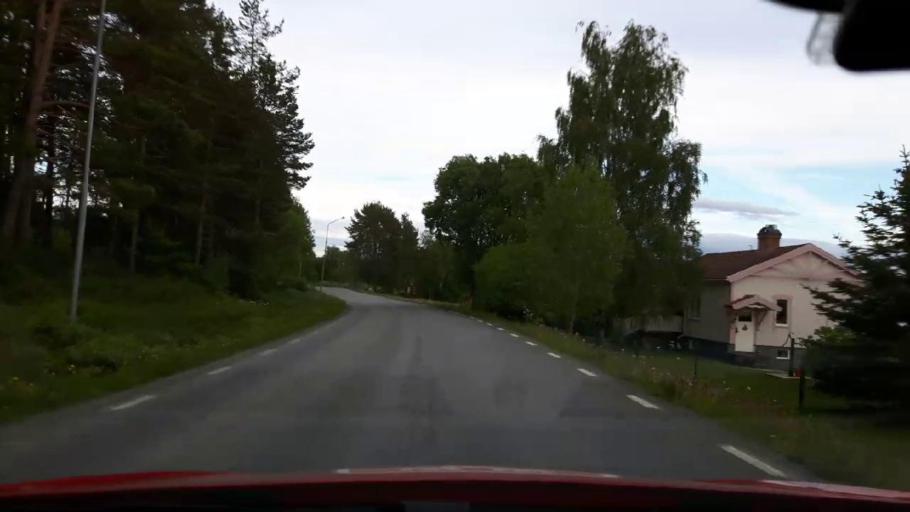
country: SE
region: Jaemtland
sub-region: OEstersunds Kommun
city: Ostersund
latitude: 63.0529
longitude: 14.4503
